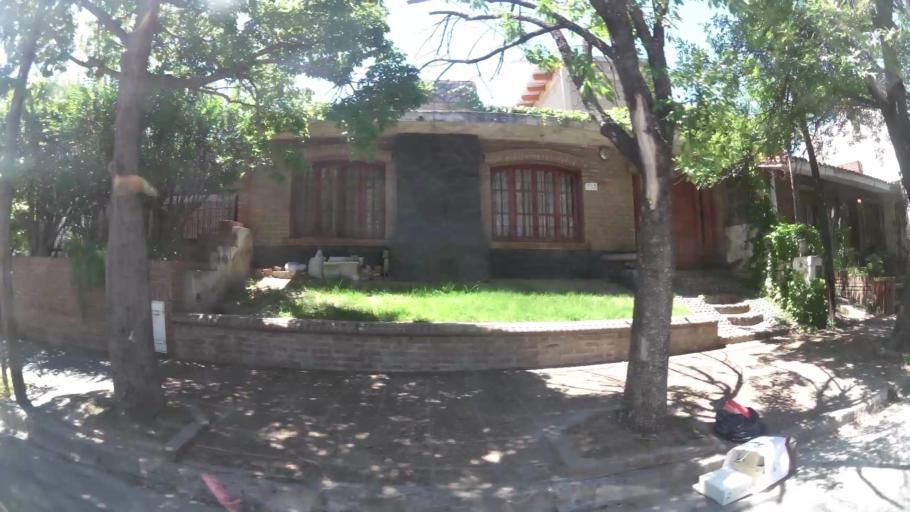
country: AR
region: Cordoba
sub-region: Departamento de Capital
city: Cordoba
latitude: -31.4149
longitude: -64.2042
